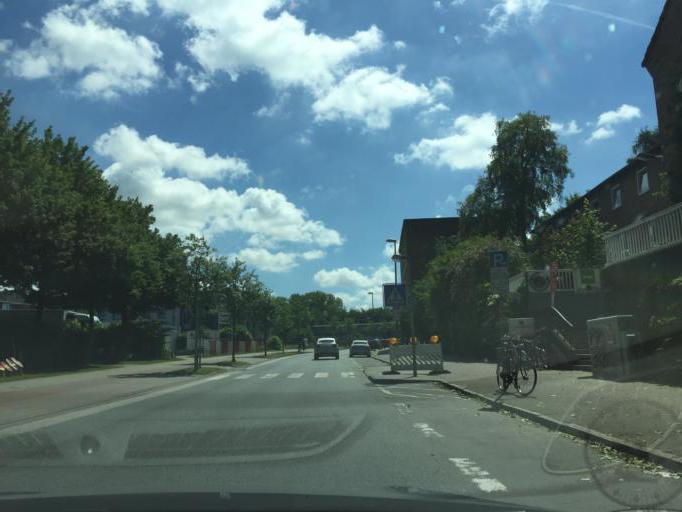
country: DE
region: Schleswig-Holstein
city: Flensburg
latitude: 54.7798
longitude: 9.4379
